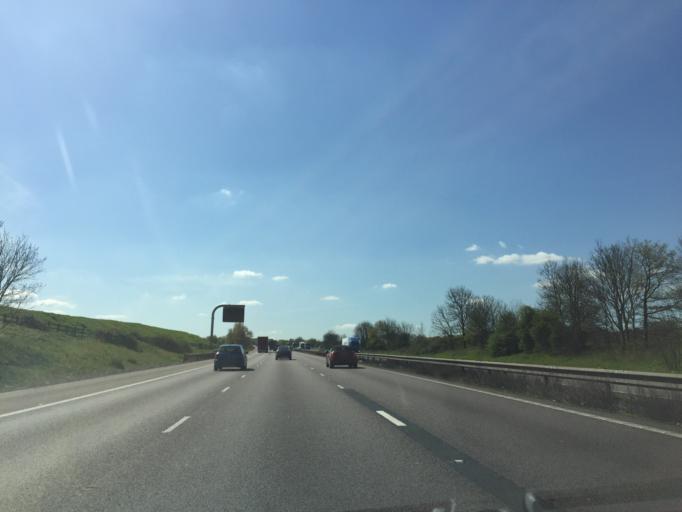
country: GB
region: England
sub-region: Essex
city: Epping
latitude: 51.7186
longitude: 0.1430
